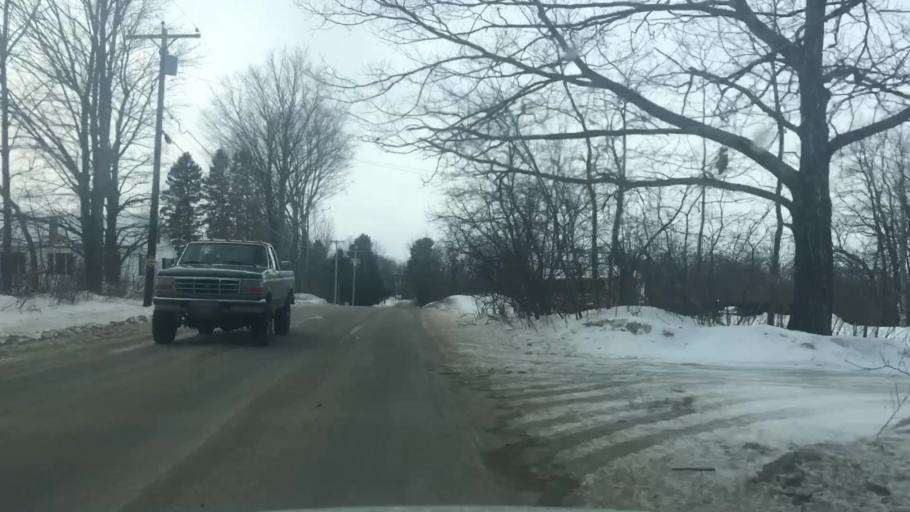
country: US
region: Maine
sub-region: Hancock County
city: Orland
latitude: 44.5721
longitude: -68.7337
